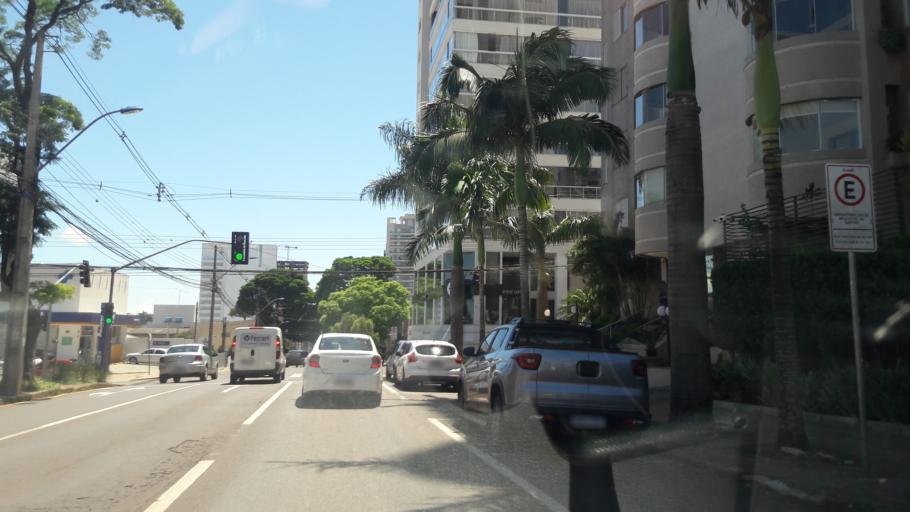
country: BR
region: Parana
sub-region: Cascavel
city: Cascavel
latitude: -24.9502
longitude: -53.4527
